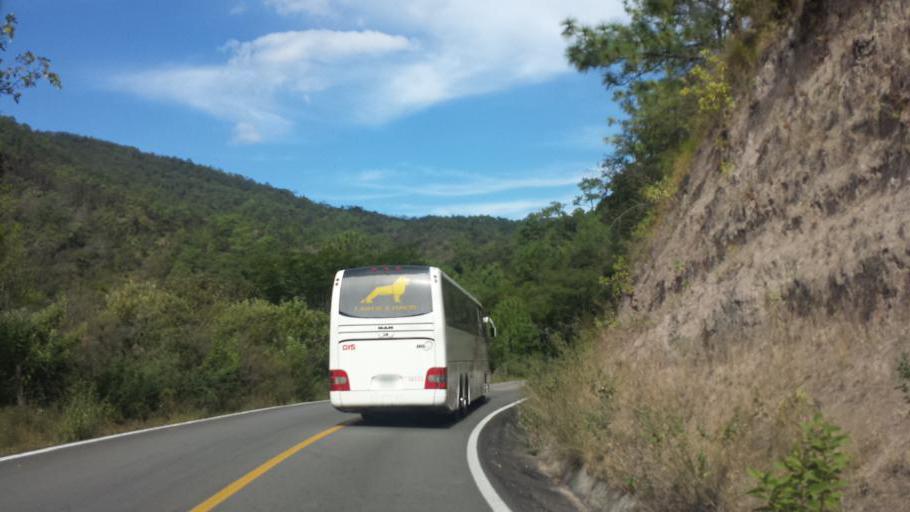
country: MX
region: Oaxaca
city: San Francisco Sola
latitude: 16.4532
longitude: -97.0319
